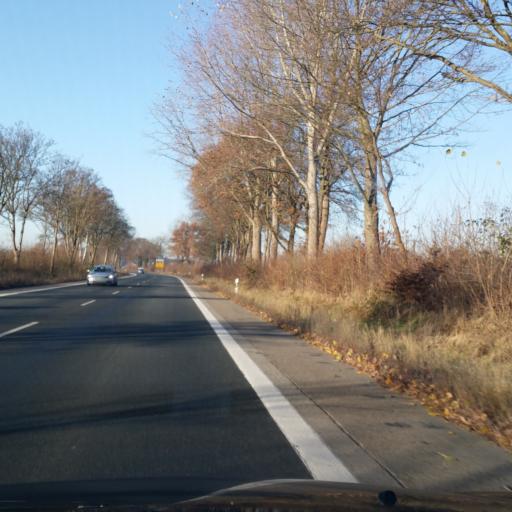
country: DE
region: North Rhine-Westphalia
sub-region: Regierungsbezirk Munster
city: Isselburg
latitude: 51.8204
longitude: 6.4585
